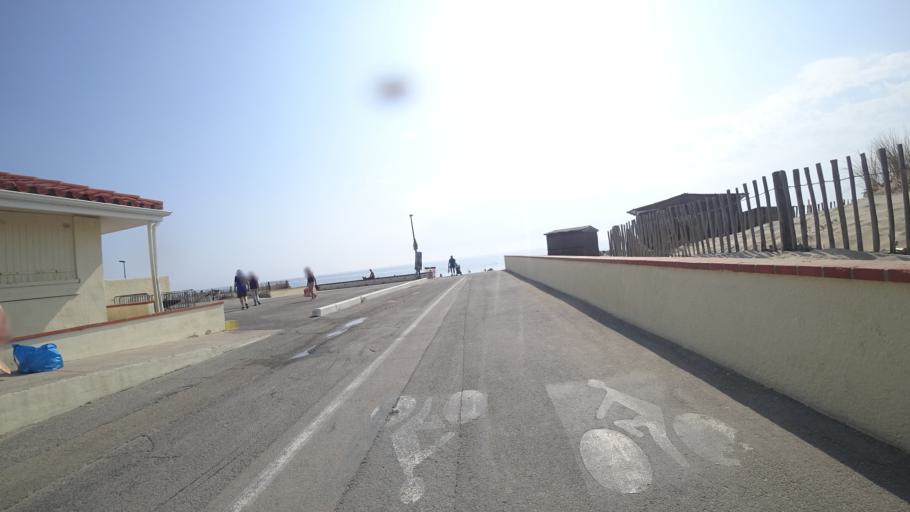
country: FR
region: Languedoc-Roussillon
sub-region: Departement des Pyrenees-Orientales
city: Saint-Cyprien-Plage
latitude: 42.6322
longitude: 3.0353
